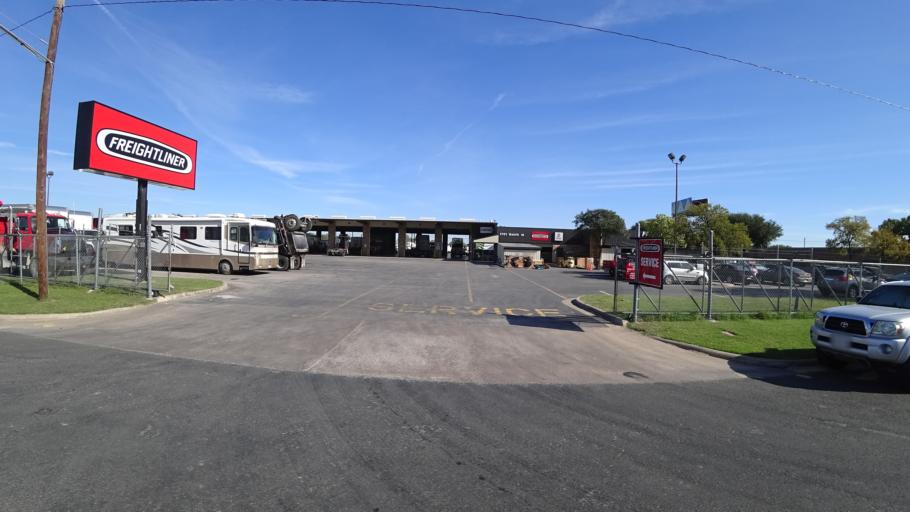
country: US
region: Texas
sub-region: Travis County
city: Austin
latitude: 30.2586
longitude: -97.6779
